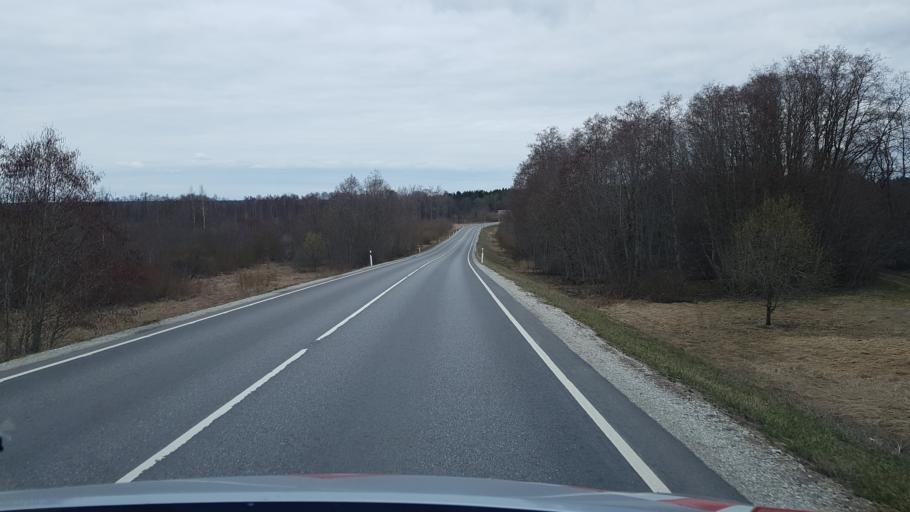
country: EE
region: Ida-Virumaa
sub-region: Narva-Joesuu linn
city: Narva-Joesuu
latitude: 59.4078
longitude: 28.0672
